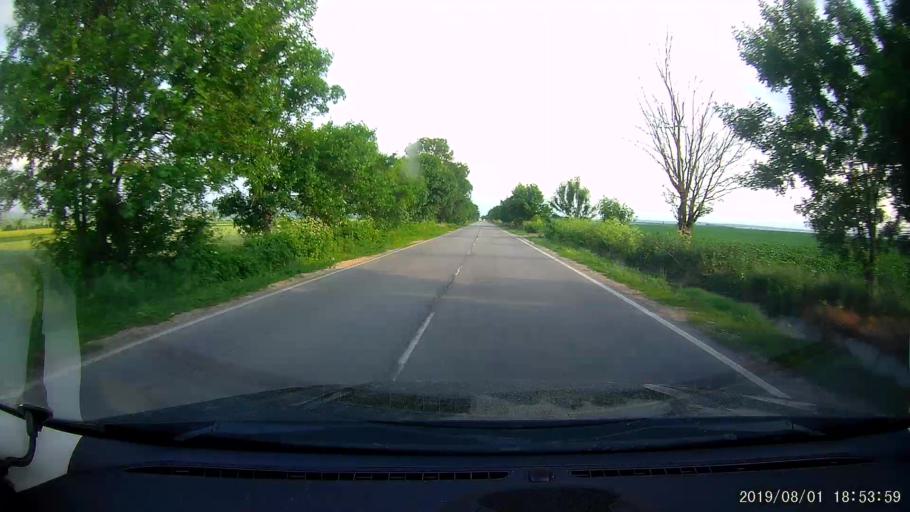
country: BG
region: Shumen
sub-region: Obshtina Shumen
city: Shumen
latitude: 43.2098
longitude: 26.9988
